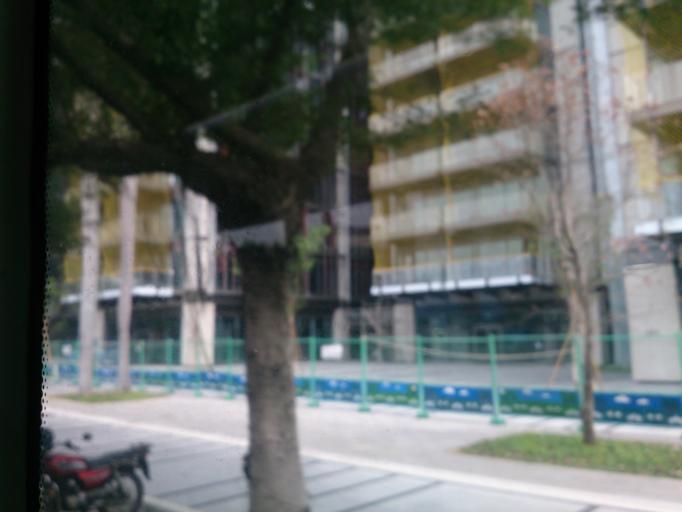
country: TW
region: Taipei
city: Taipei
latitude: 25.0928
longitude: 121.5280
